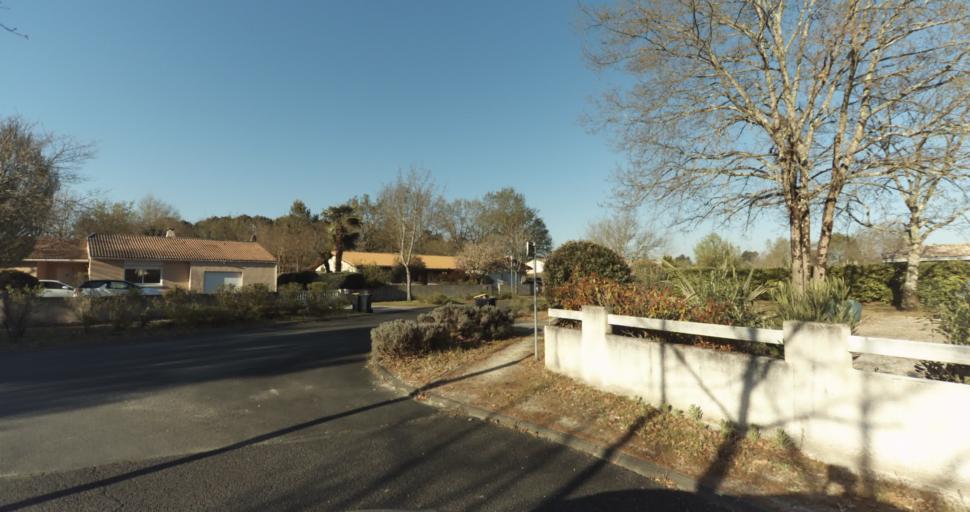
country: FR
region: Aquitaine
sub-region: Departement de la Gironde
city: Martignas-sur-Jalle
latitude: 44.8097
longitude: -0.7954
